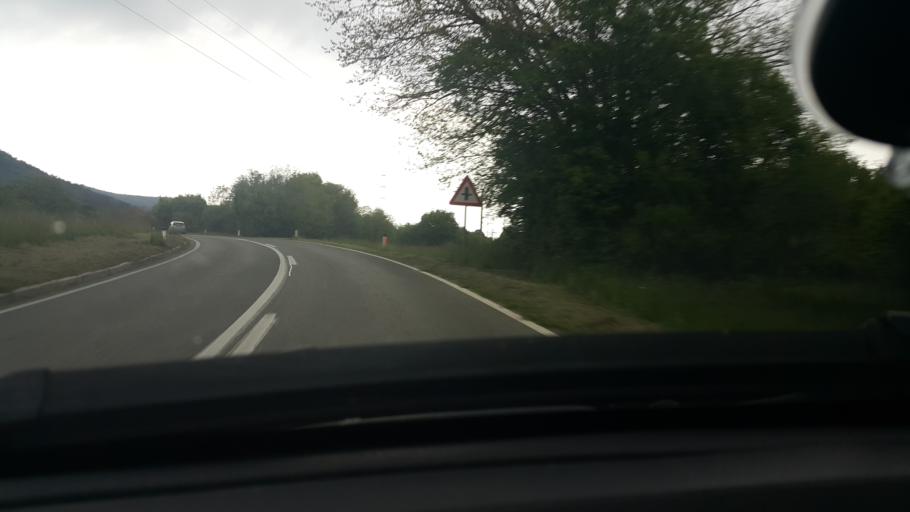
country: SI
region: Divaca
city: Divaca
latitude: 45.7021
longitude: 13.9325
